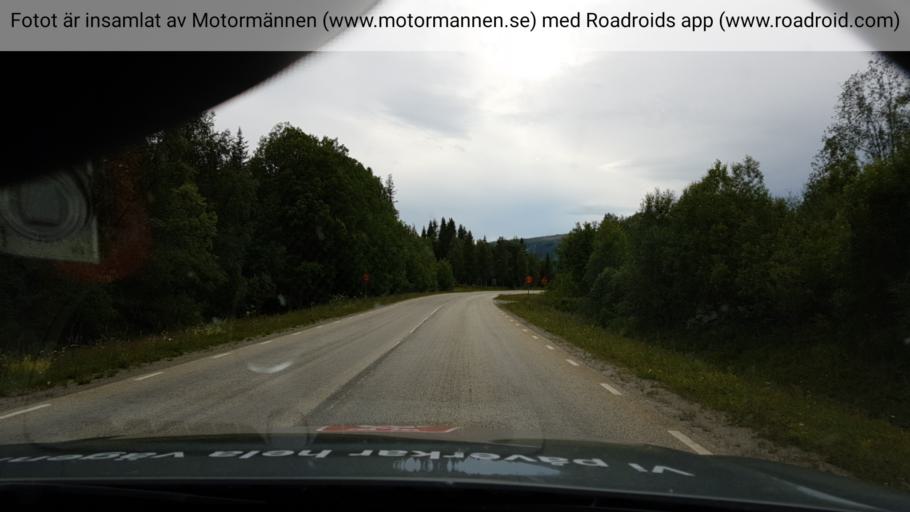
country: SE
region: Jaemtland
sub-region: Bergs Kommun
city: Hoverberg
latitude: 62.5327
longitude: 14.2089
